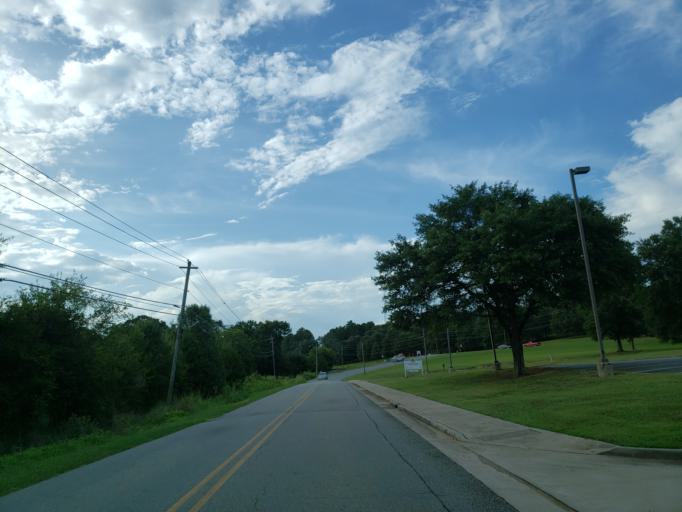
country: US
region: Georgia
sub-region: Bartow County
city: Euharlee
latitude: 34.1484
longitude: -84.9353
